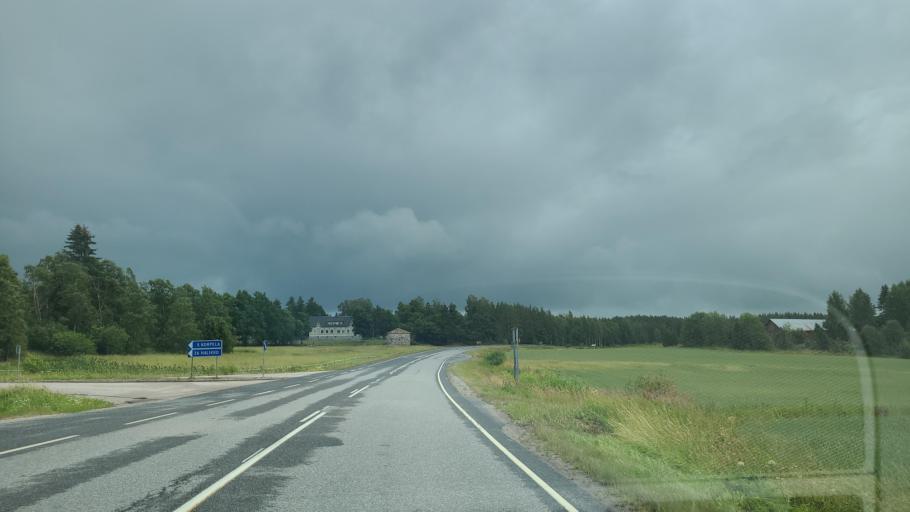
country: FI
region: Varsinais-Suomi
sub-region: Turku
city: Sauvo
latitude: 60.3310
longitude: 22.7123
